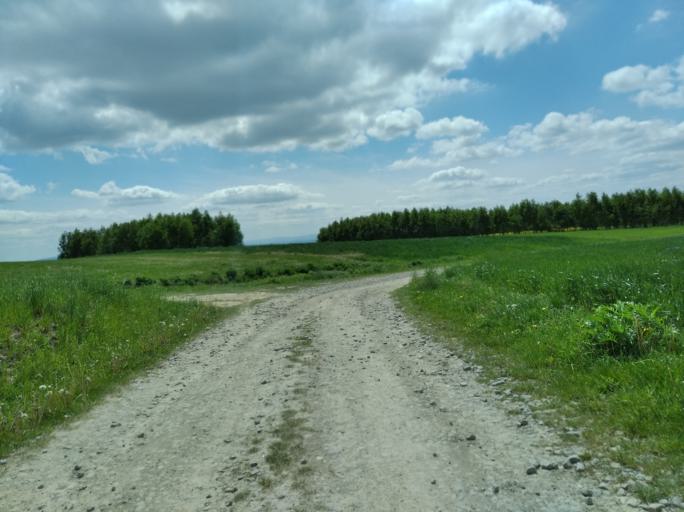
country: PL
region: Subcarpathian Voivodeship
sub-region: Powiat ropczycko-sedziszowski
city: Wielopole Skrzynskie
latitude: 49.8982
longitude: 21.5794
